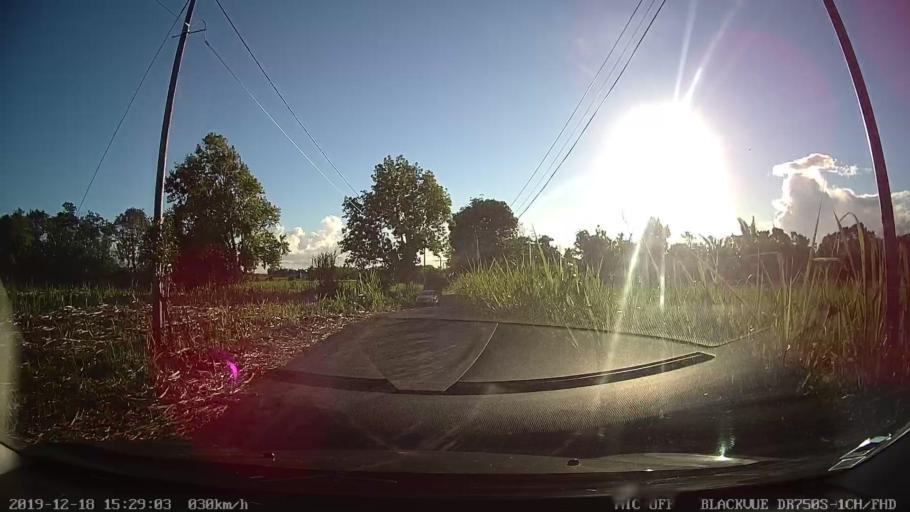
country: RE
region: Reunion
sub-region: Reunion
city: Bras-Panon
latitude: -20.9987
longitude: 55.6597
